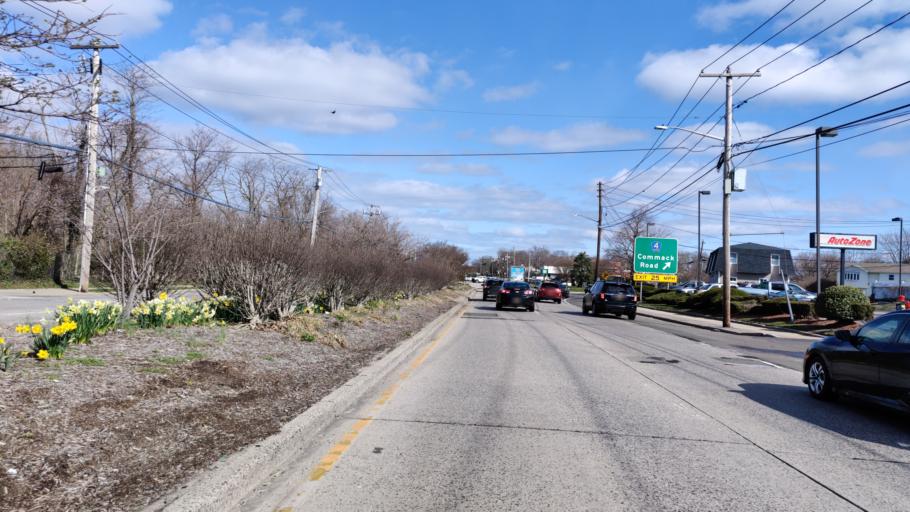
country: US
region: New York
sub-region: Suffolk County
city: Deer Park
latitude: 40.7409
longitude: -73.3213
